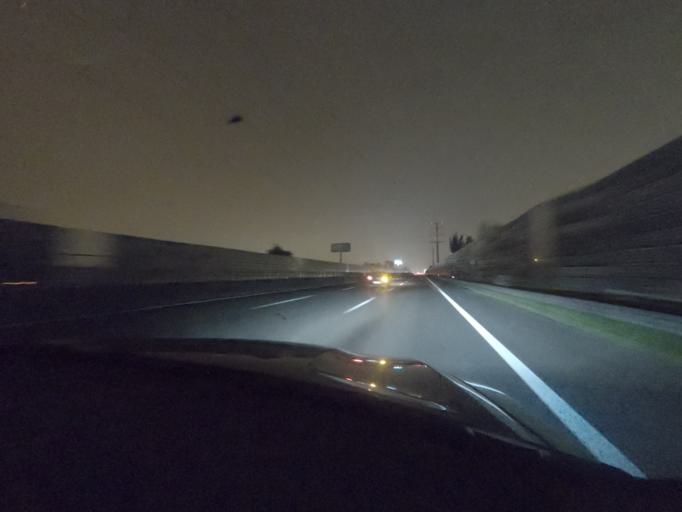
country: PT
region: Lisbon
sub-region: Loures
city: Sao Joao da Talha
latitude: 38.8316
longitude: -9.0971
